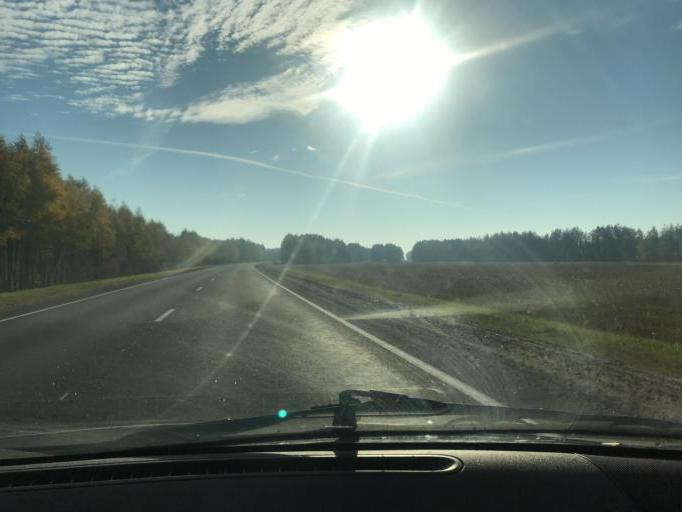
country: BY
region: Brest
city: Drahichyn
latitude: 52.1865
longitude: 25.2892
